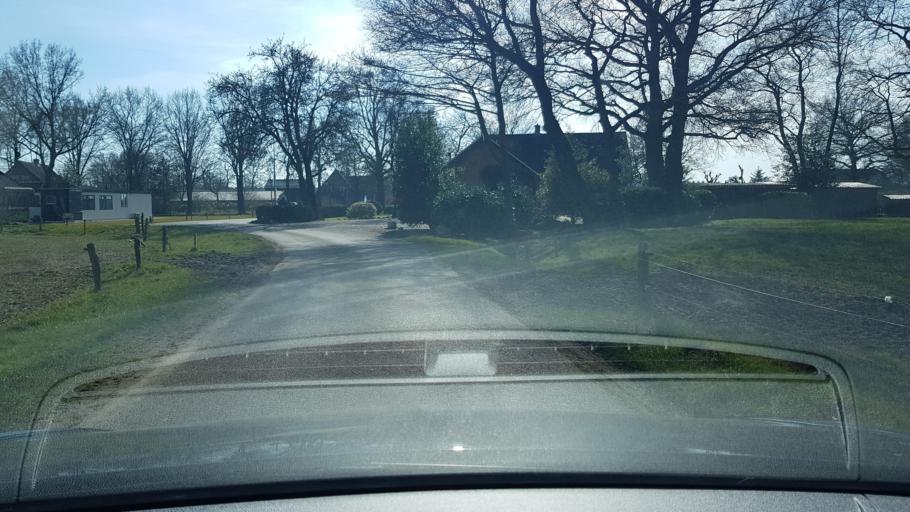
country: NL
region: Gelderland
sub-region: Gemeente Epe
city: Emst
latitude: 52.3370
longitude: 5.9558
